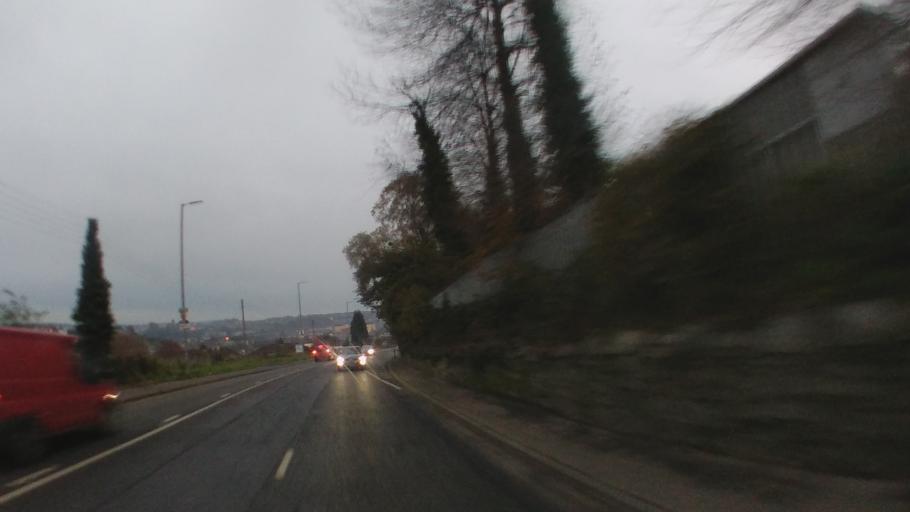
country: GB
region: Northern Ireland
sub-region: Newry and Mourne District
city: Newry
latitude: 54.1801
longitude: -6.3489
